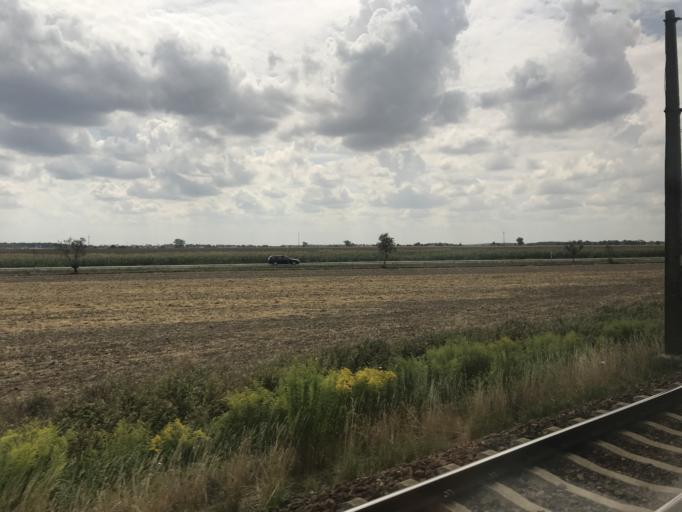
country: PL
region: Greater Poland Voivodeship
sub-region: Powiat poznanski
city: Dopiewo
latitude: 52.3606
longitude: 16.6973
